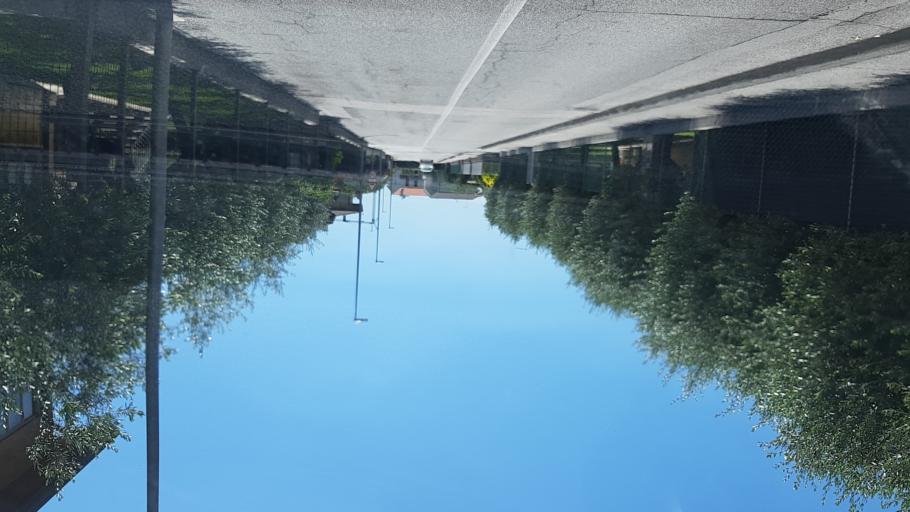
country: IT
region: Veneto
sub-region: Provincia di Vicenza
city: Pove del Grappa
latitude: 45.7952
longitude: 11.7316
